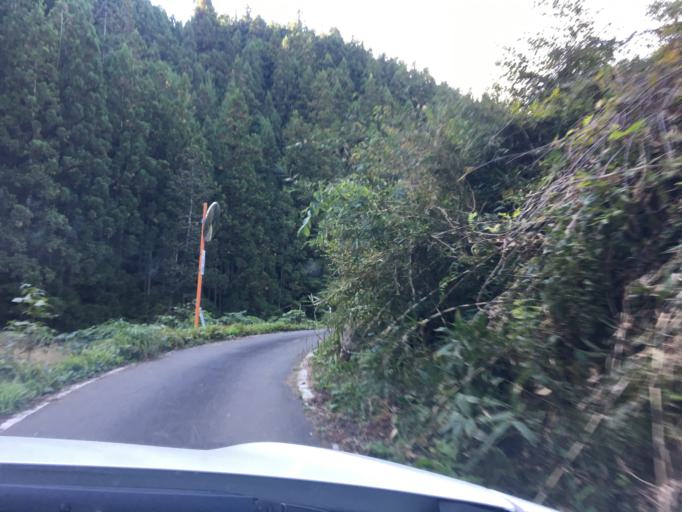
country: JP
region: Fukushima
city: Ishikawa
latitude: 37.1614
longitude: 140.5090
